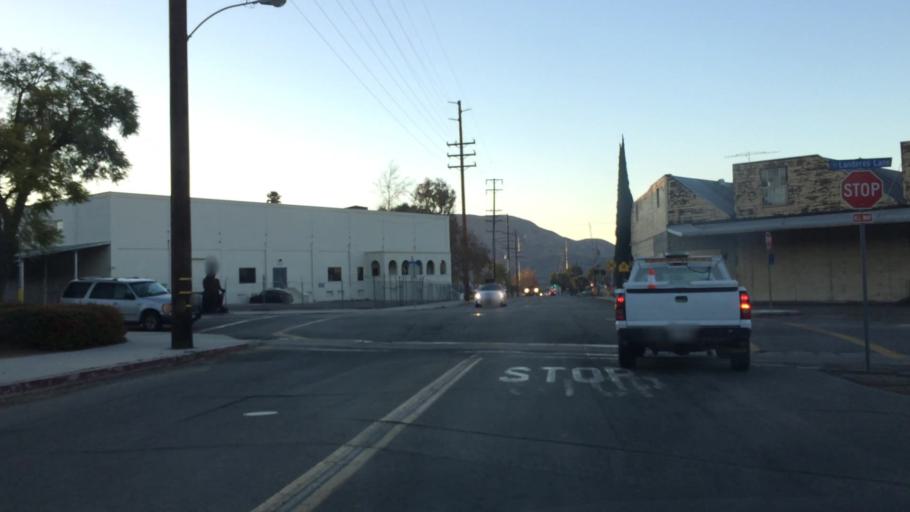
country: US
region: California
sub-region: Ventura County
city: Fillmore
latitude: 34.4004
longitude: -118.9186
